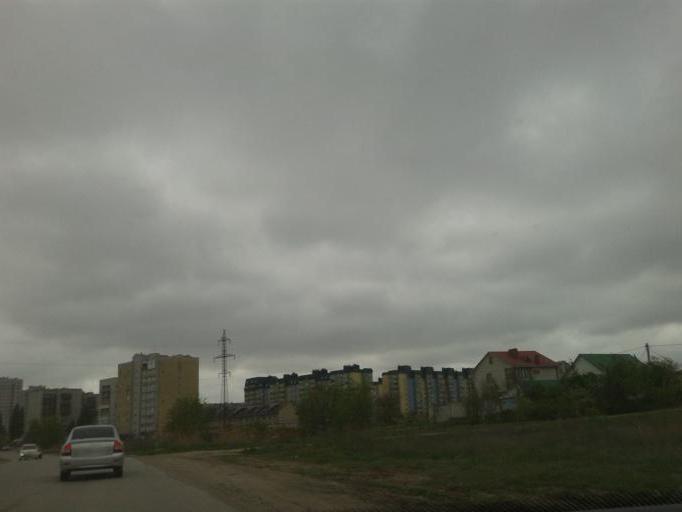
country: RU
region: Volgograd
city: Volgograd
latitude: 48.7639
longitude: 44.4976
